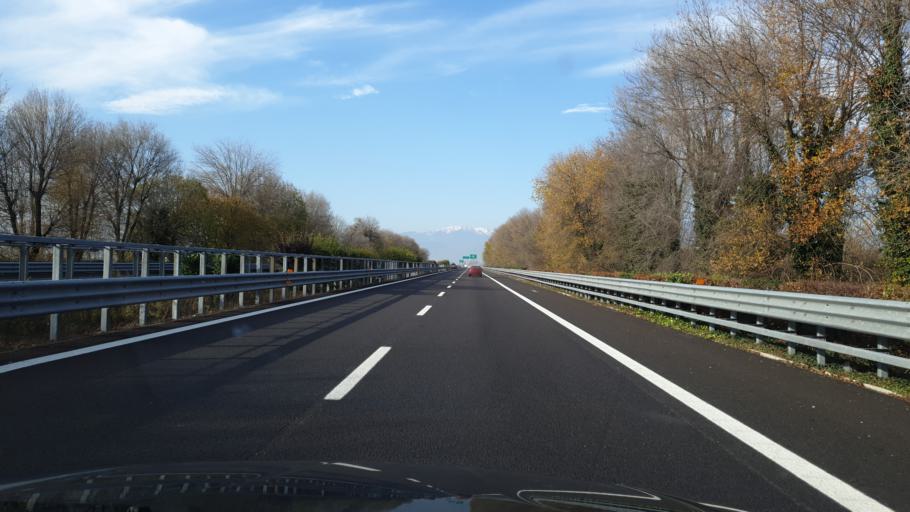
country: IT
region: Veneto
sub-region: Provincia di Vicenza
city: Novoledo
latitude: 45.6578
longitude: 11.5278
